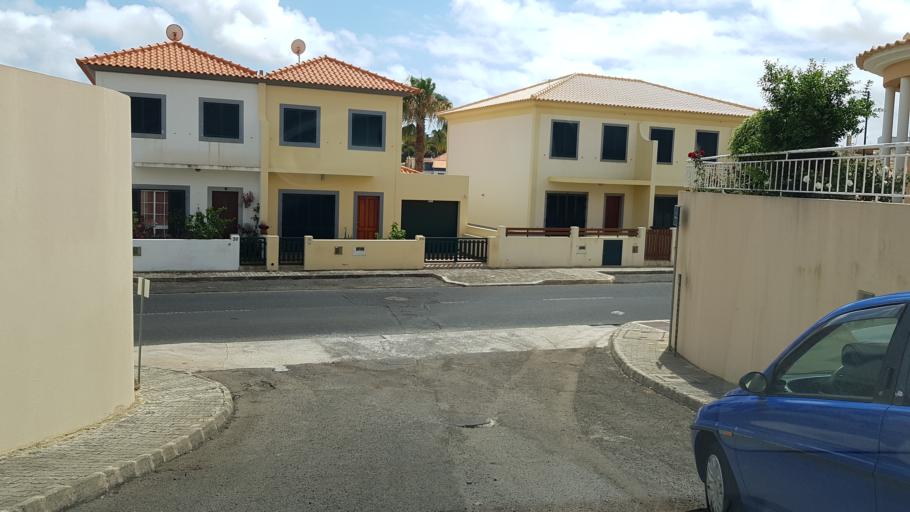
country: PT
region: Madeira
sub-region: Porto Santo
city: Vila de Porto Santo
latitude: 33.0614
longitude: -16.3418
